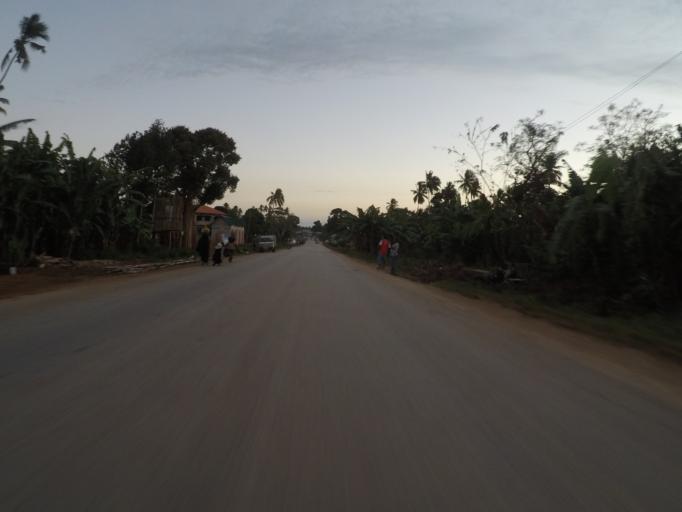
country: TZ
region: Zanzibar Central/South
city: Koani
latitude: -6.0482
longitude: 39.2265
